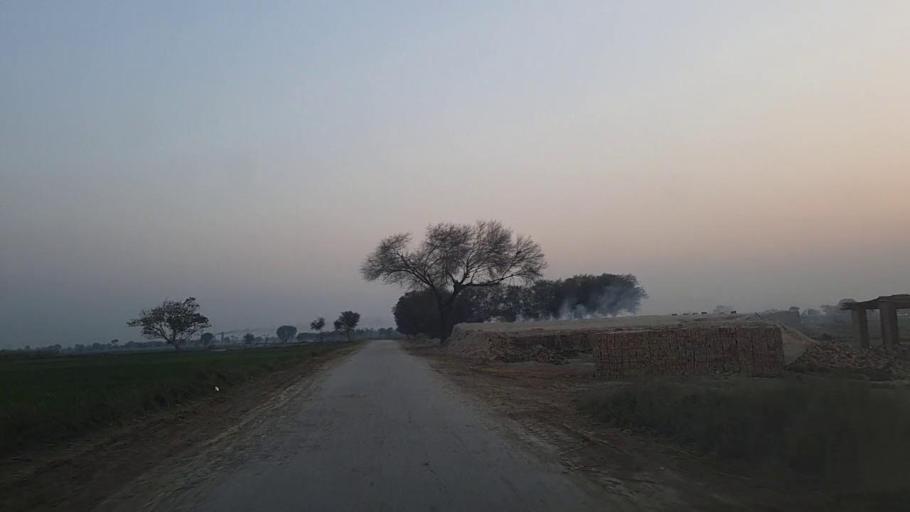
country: PK
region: Sindh
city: Naushahro Firoz
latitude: 26.8639
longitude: 68.0475
